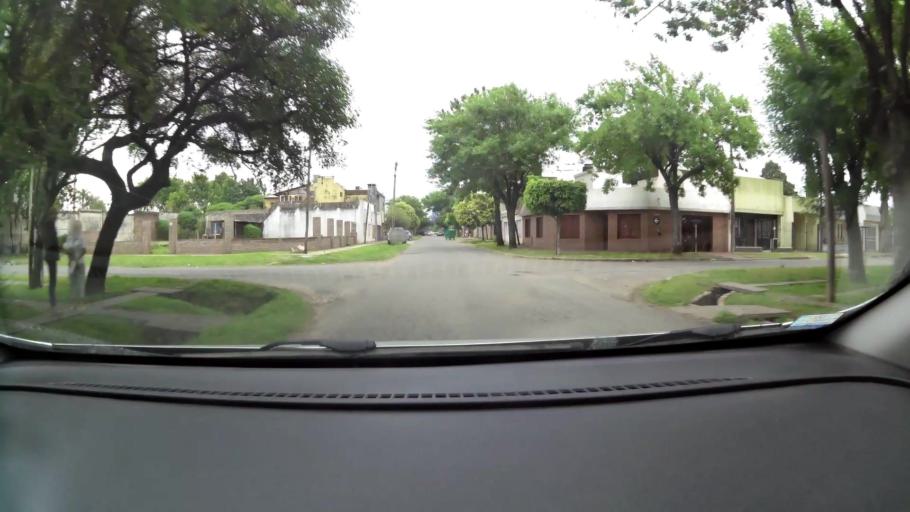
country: AR
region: Santa Fe
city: Granadero Baigorria
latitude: -32.8949
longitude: -60.6995
